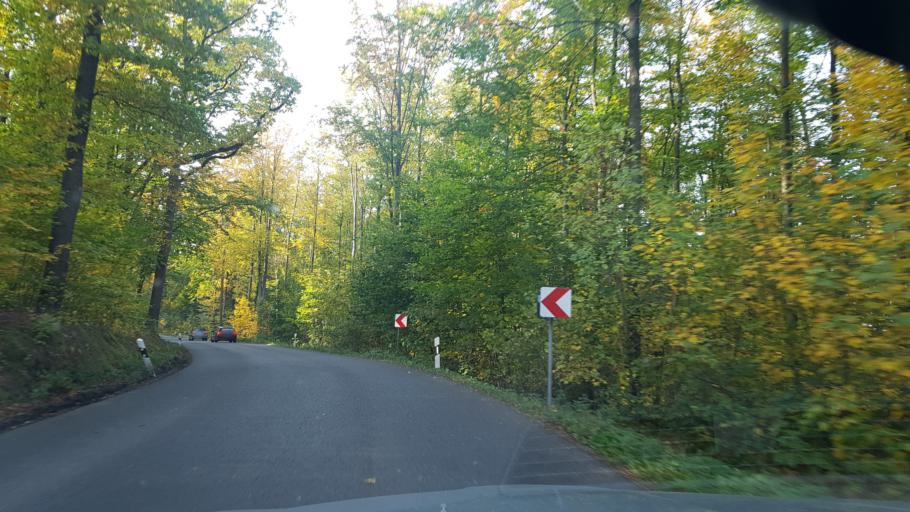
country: DE
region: Saxony
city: Struppen
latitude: 50.9268
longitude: 14.0432
